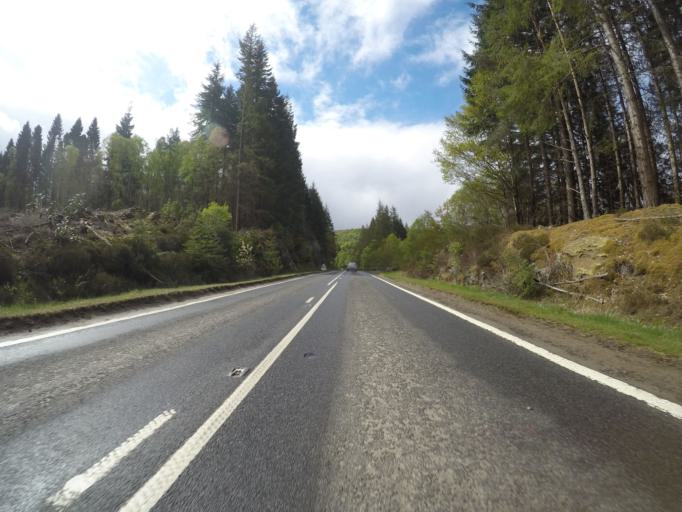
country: GB
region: Scotland
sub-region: Highland
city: Spean Bridge
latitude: 57.0694
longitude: -4.8316
